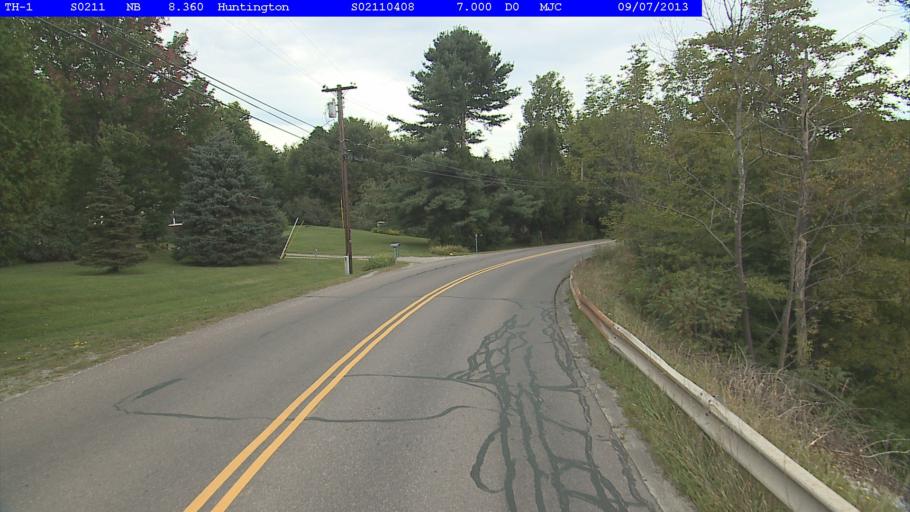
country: US
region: Vermont
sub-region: Chittenden County
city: Hinesburg
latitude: 44.3196
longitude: -72.9896
